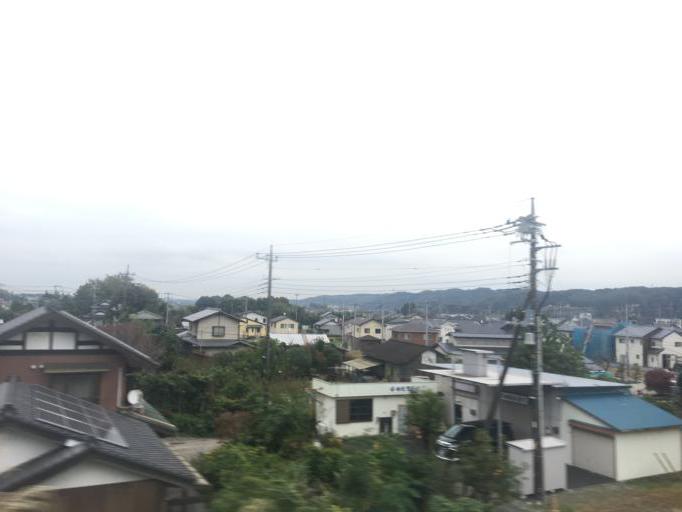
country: JP
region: Saitama
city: Hanno
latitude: 35.8396
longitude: 139.3341
